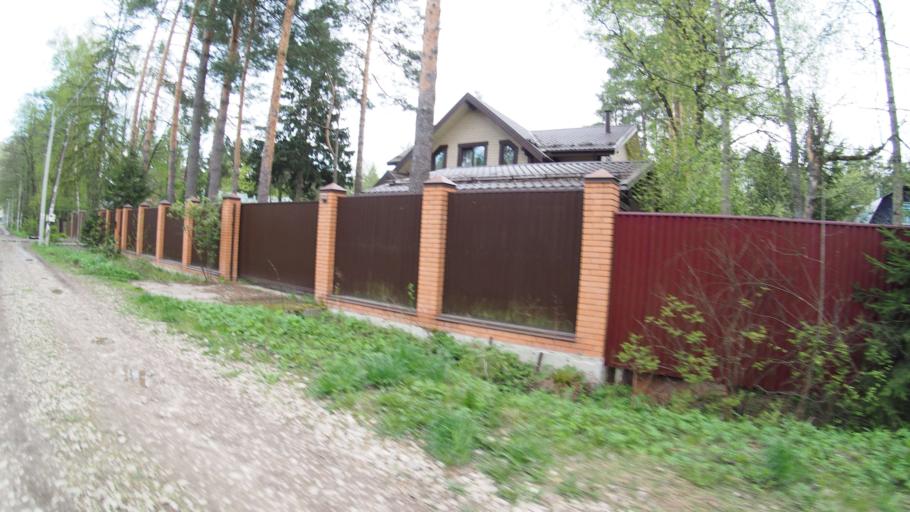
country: RU
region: Moskovskaya
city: Kratovo
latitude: 55.5957
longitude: 38.2004
